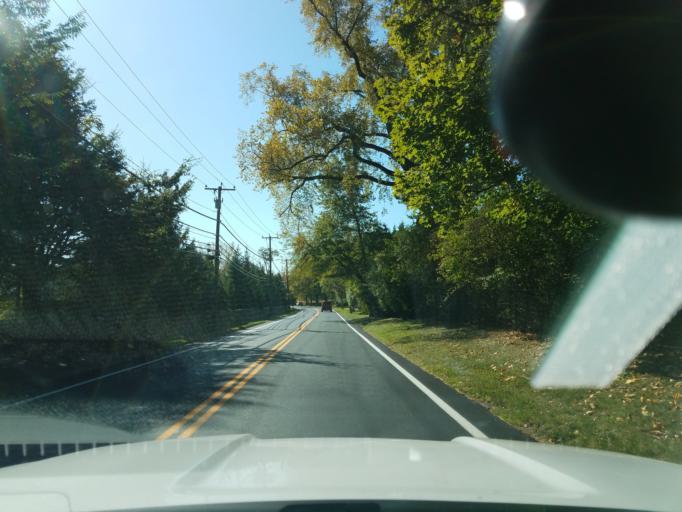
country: US
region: Connecticut
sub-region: Fairfield County
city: Cos Cob
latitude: 41.0761
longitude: -73.6238
